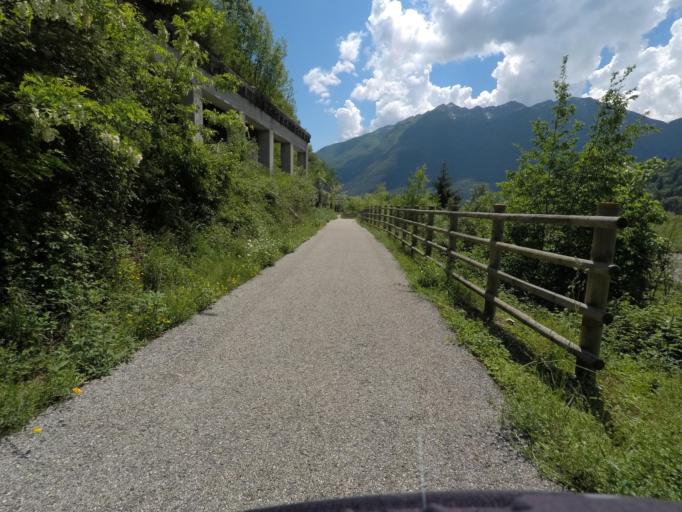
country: IT
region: Friuli Venezia Giulia
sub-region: Provincia di Udine
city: Villa Santina
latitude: 46.4236
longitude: 12.9053
